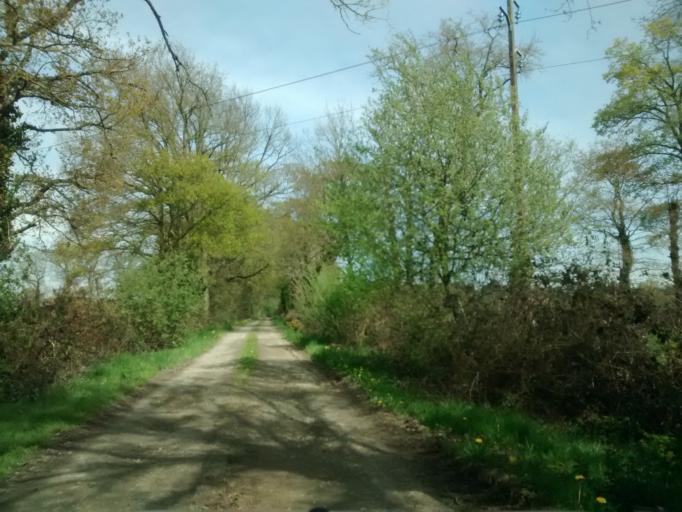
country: FR
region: Brittany
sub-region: Departement d'Ille-et-Vilaine
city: Fouillard
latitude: 48.1641
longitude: -1.5969
